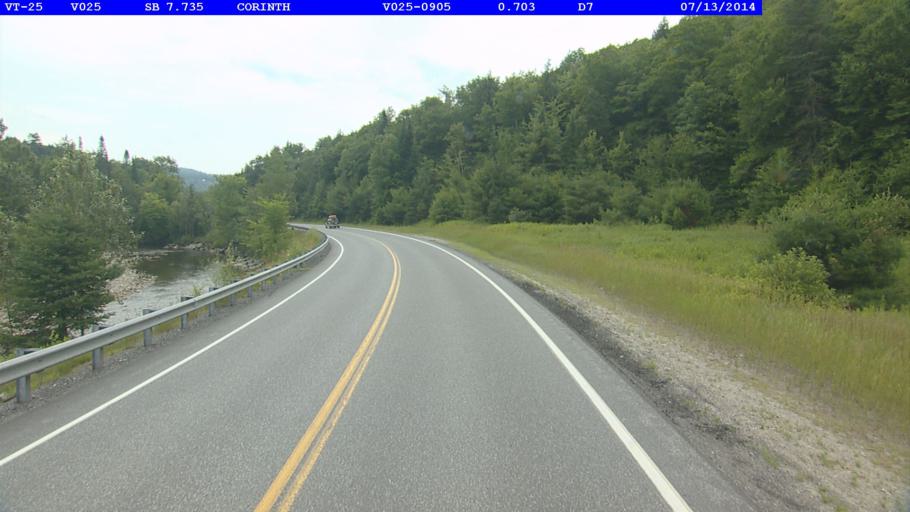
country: US
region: New Hampshire
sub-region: Grafton County
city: Haverhill
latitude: 44.0469
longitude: -72.2153
